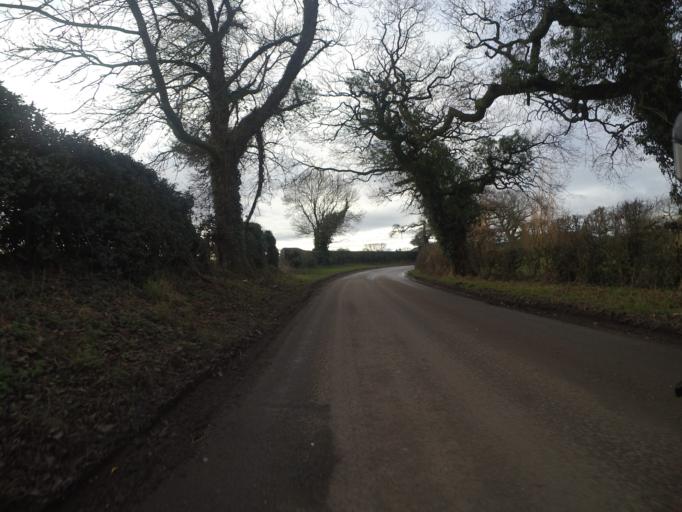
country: GB
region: England
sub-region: Cheshire West and Chester
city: Tiverton
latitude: 53.1193
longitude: -2.6684
